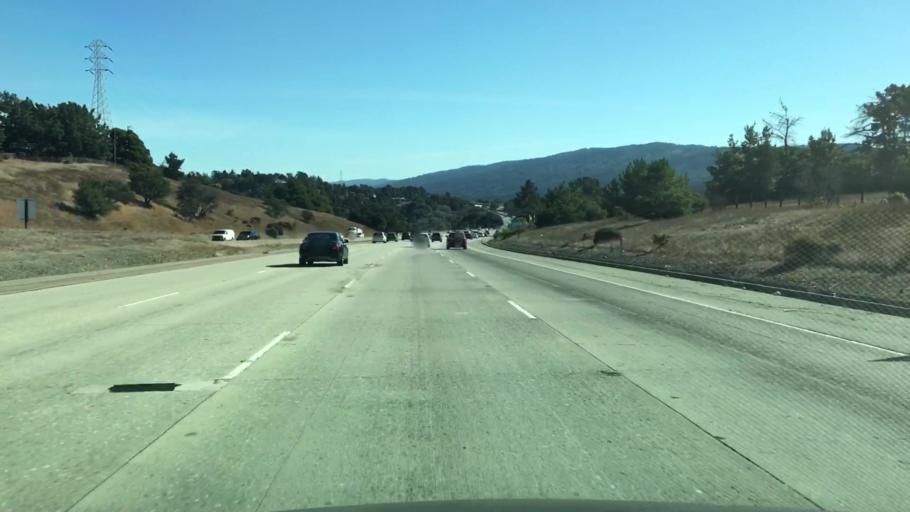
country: US
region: California
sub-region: San Mateo County
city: Highlands-Baywood Park
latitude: 37.5354
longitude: -122.3632
